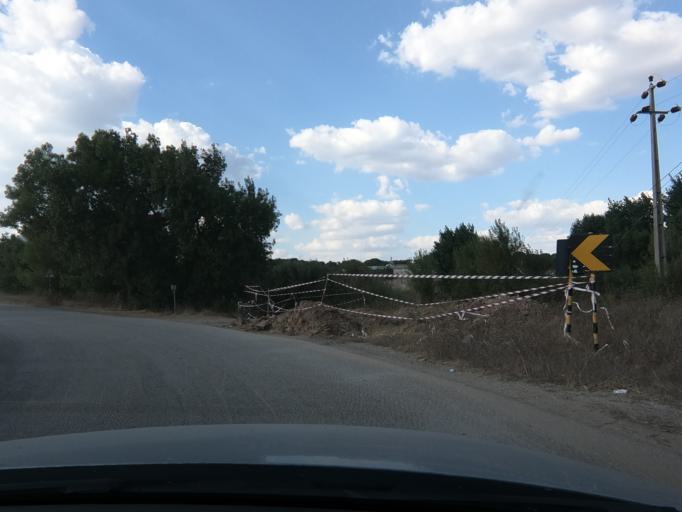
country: PT
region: Setubal
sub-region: Alcacer do Sal
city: Alcacer do Sal
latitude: 38.2510
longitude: -8.3584
